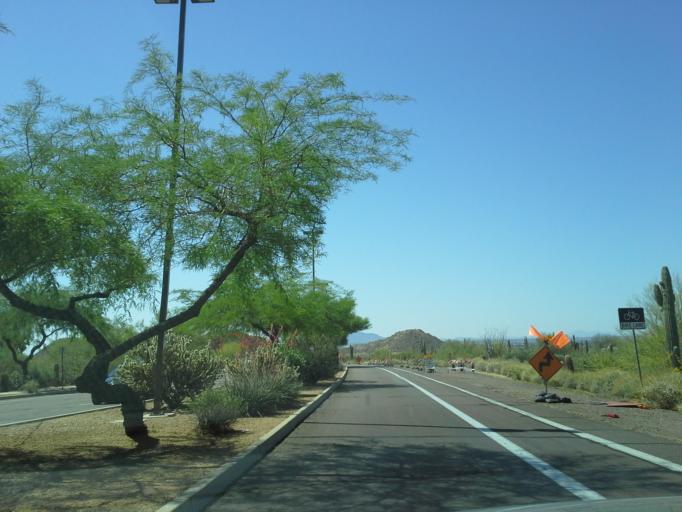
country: US
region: Arizona
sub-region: Pinal County
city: Apache Junction
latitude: 33.4609
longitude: -111.6321
